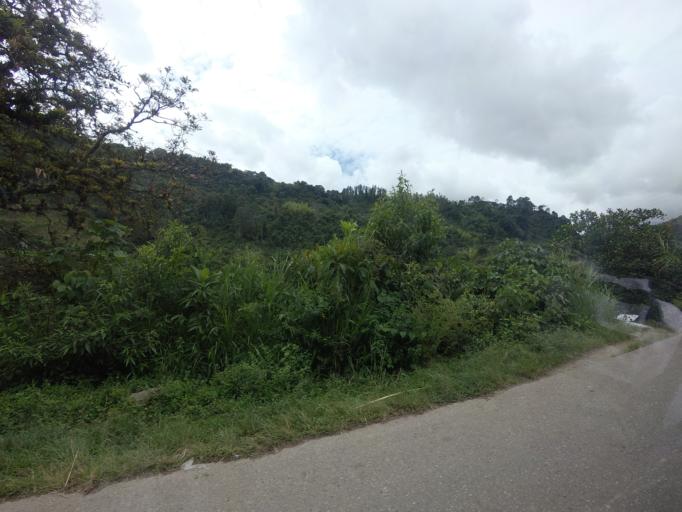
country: CO
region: Huila
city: San Agustin
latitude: 1.9264
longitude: -76.3003
